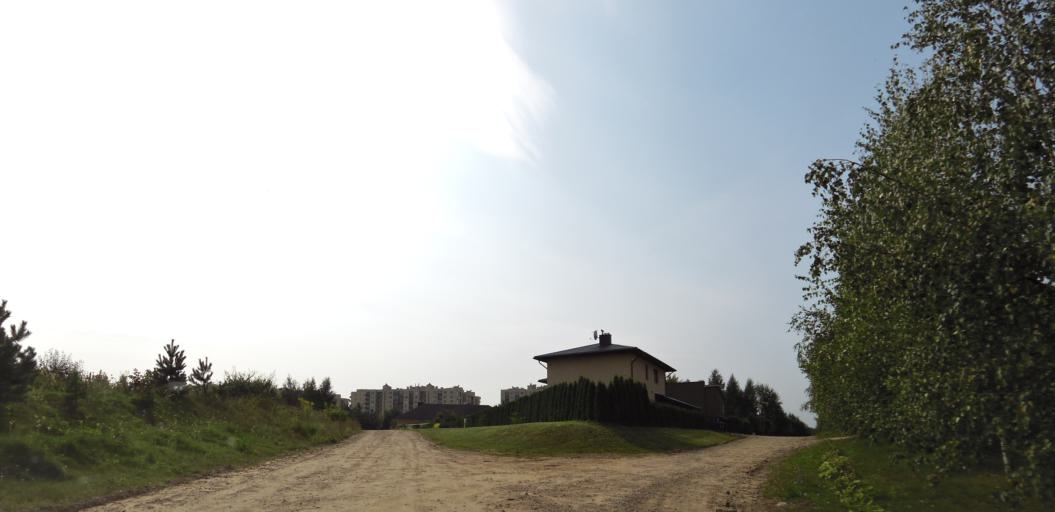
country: LT
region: Vilnius County
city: Pasilaiciai
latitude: 54.7460
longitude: 25.2307
